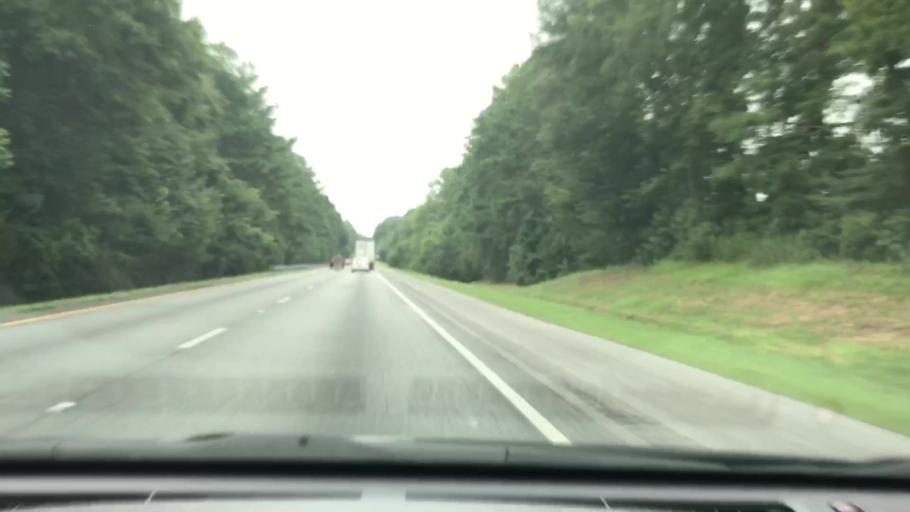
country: US
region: Georgia
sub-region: Morgan County
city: Madison
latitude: 33.5779
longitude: -83.5453
